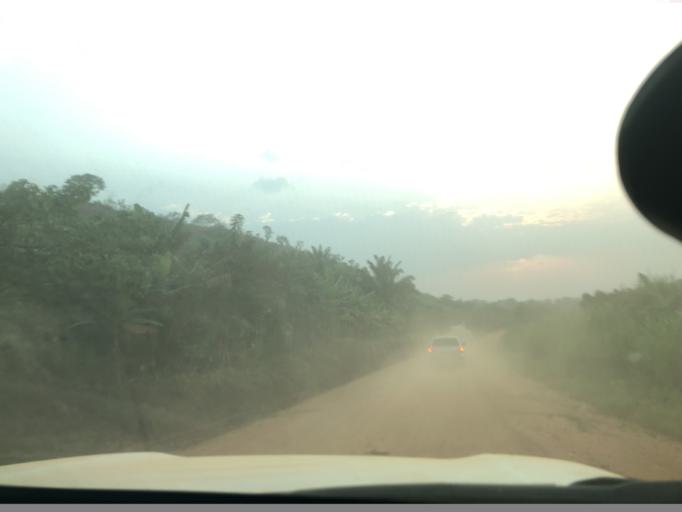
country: CD
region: Nord Kivu
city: Beni
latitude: 0.3752
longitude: 29.6081
